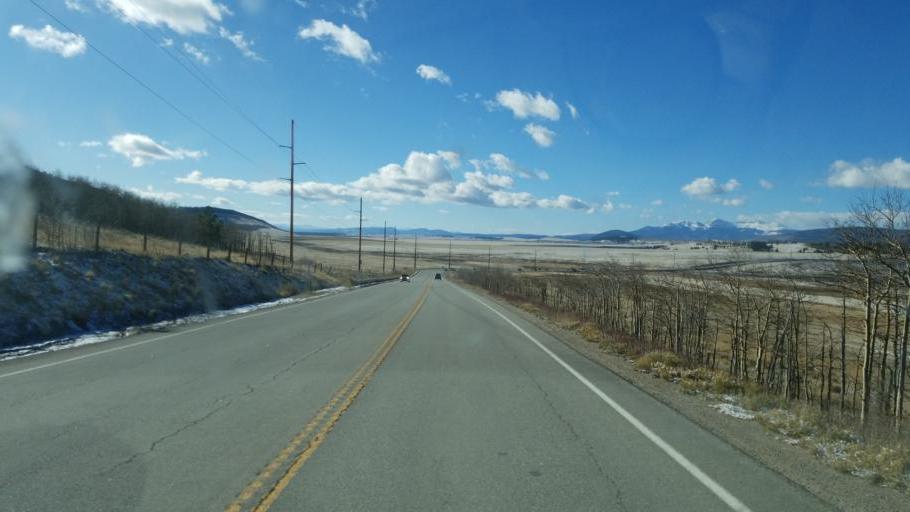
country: US
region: Colorado
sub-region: Park County
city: Fairplay
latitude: 39.2549
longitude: -105.9633
